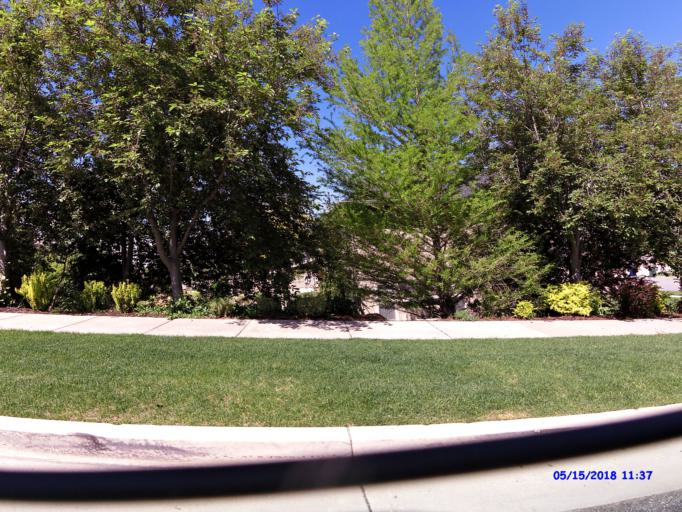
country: US
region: Utah
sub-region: Weber County
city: South Ogden
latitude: 41.1748
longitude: -111.9414
